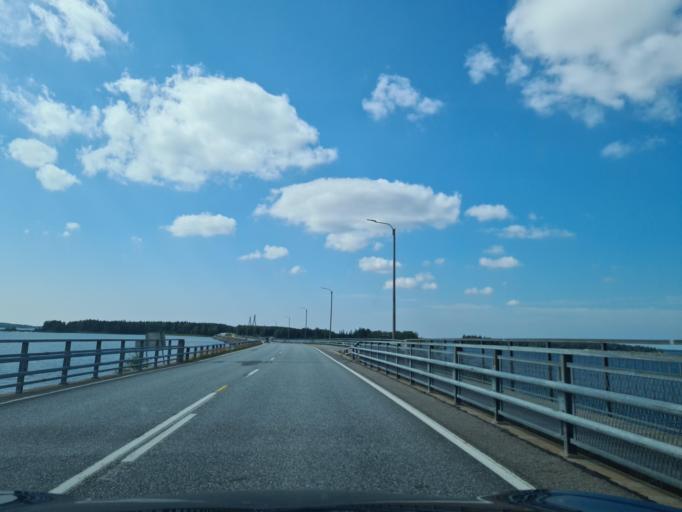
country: FI
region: Ostrobothnia
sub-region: Vaasa
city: Replot
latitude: 63.2053
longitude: 21.5171
